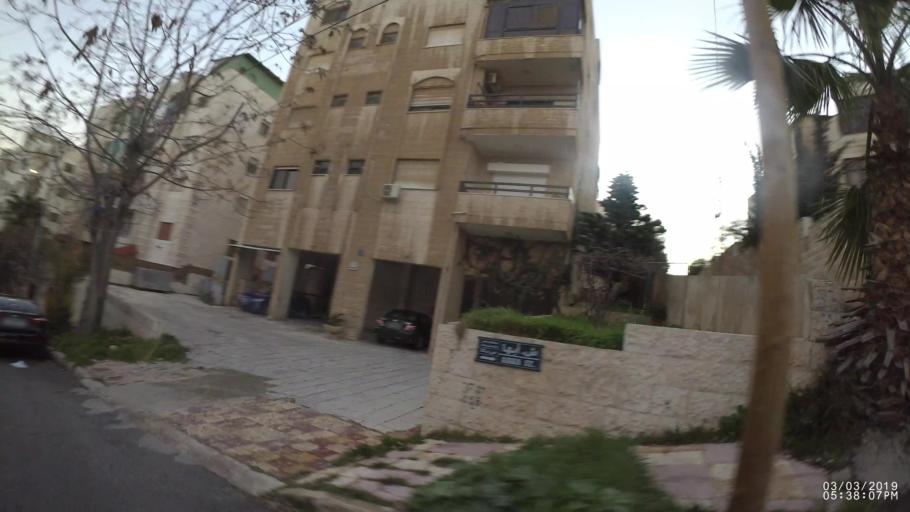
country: JO
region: Amman
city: Al Jubayhah
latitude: 31.9924
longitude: 35.8843
